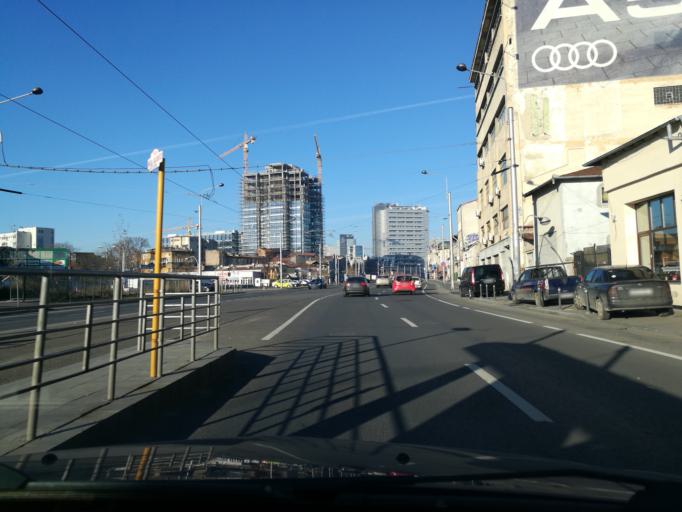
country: RO
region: Bucuresti
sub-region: Municipiul Bucuresti
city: Bucuresti
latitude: 44.4436
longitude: 26.0812
